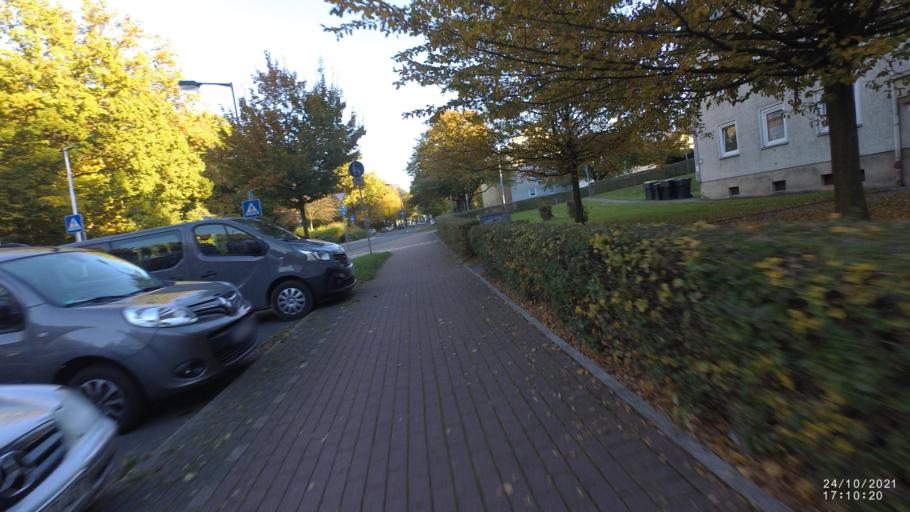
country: DE
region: North Rhine-Westphalia
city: Iserlohn
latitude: 51.3791
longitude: 7.7254
